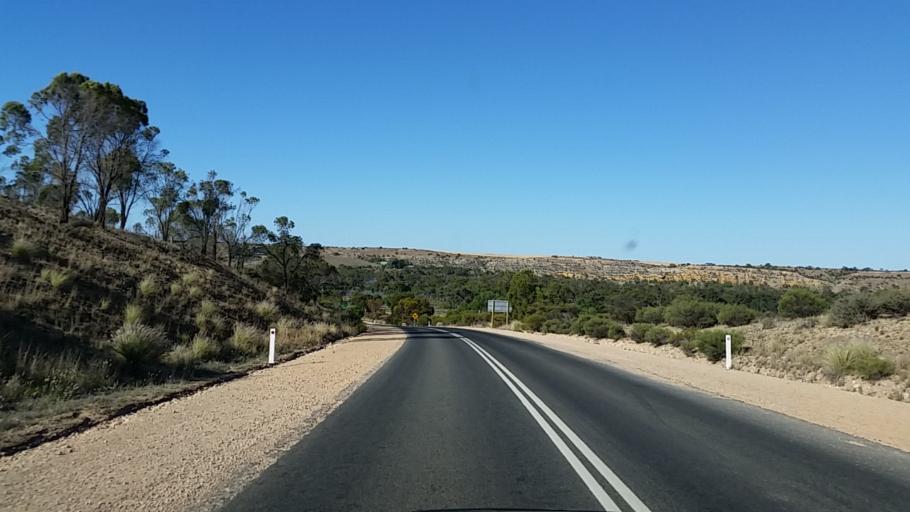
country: AU
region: South Australia
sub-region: Mid Murray
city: Mannum
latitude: -34.7558
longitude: 139.5544
